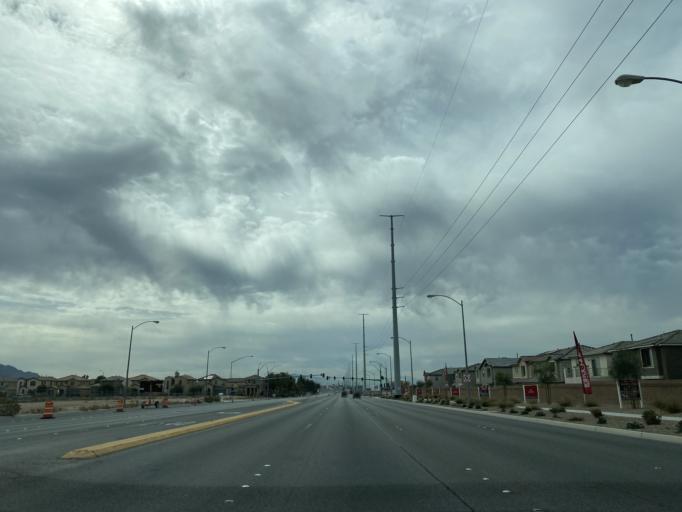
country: US
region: Nevada
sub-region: Clark County
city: Nellis Air Force Base
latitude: 36.2748
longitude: -115.0800
